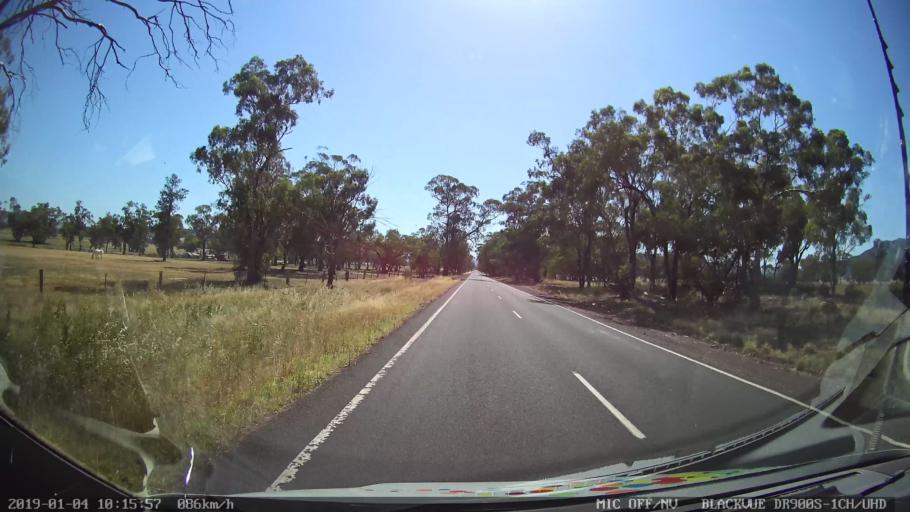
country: AU
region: New South Wales
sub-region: Cabonne
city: Canowindra
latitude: -33.3863
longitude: 148.4291
